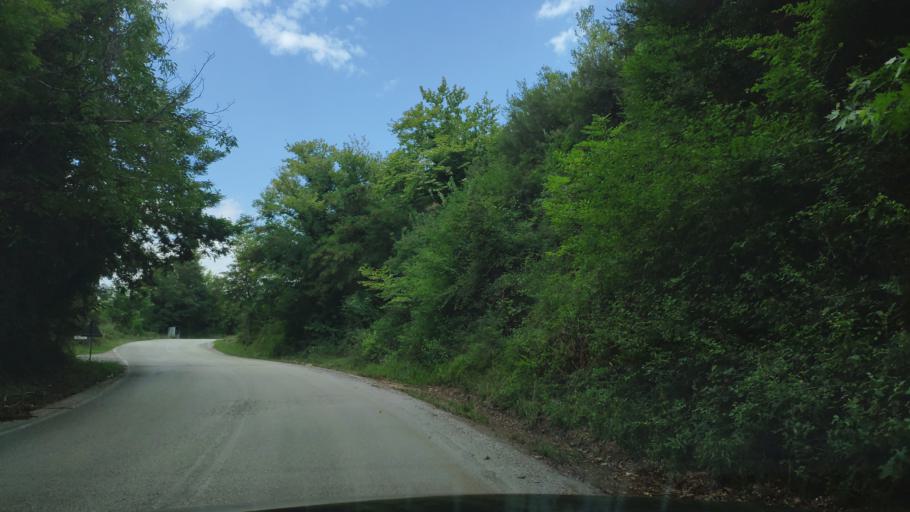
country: GR
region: Epirus
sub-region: Nomos Artas
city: Agios Dimitrios
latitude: 39.4588
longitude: 21.0372
